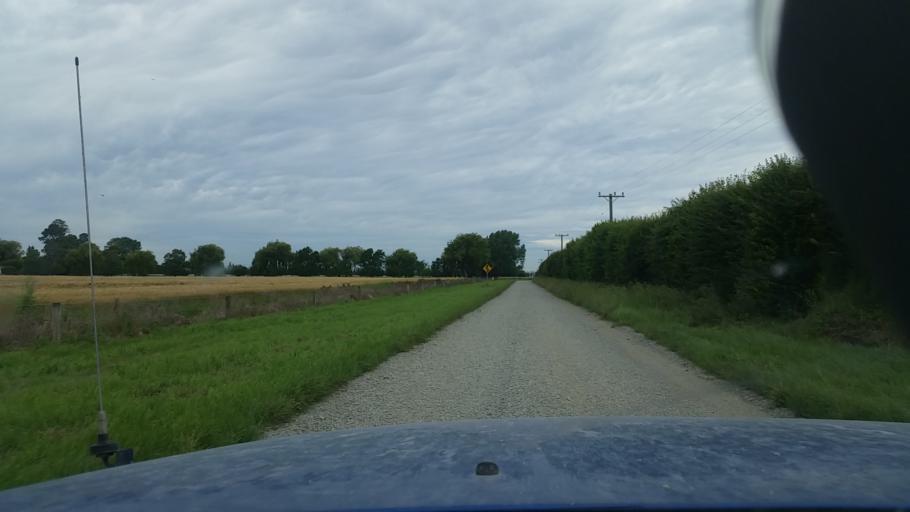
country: NZ
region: Canterbury
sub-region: Ashburton District
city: Ashburton
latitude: -43.8440
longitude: 171.6594
